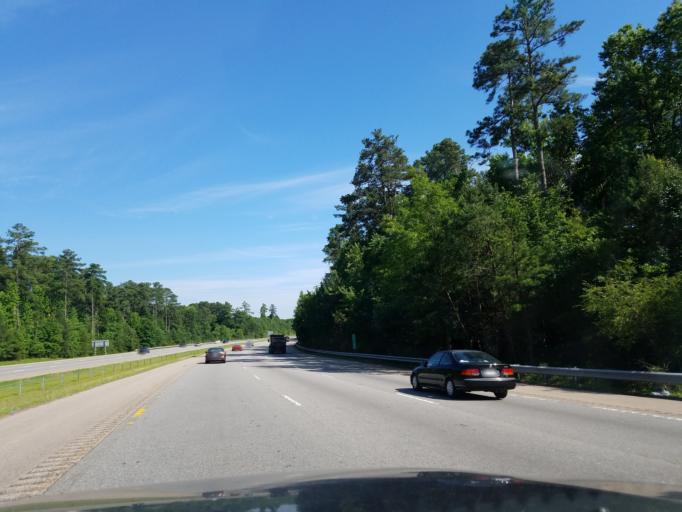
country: US
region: North Carolina
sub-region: Wake County
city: Wake Forest
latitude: 35.8906
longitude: -78.5945
